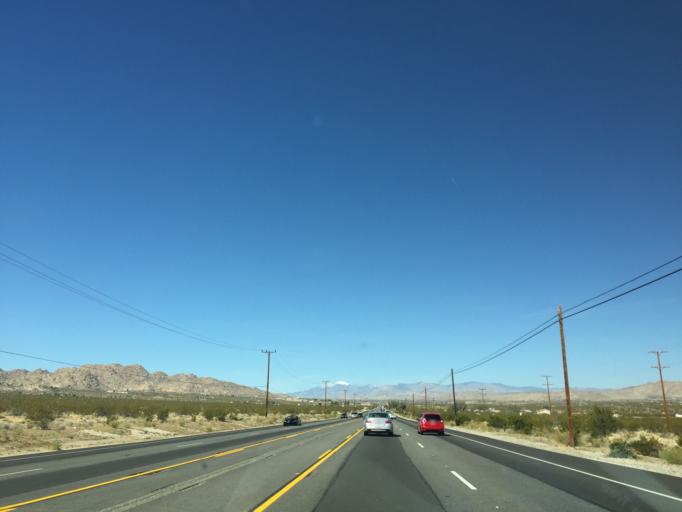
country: US
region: California
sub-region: San Bernardino County
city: Joshua Tree
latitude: 34.1352
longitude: -116.2393
